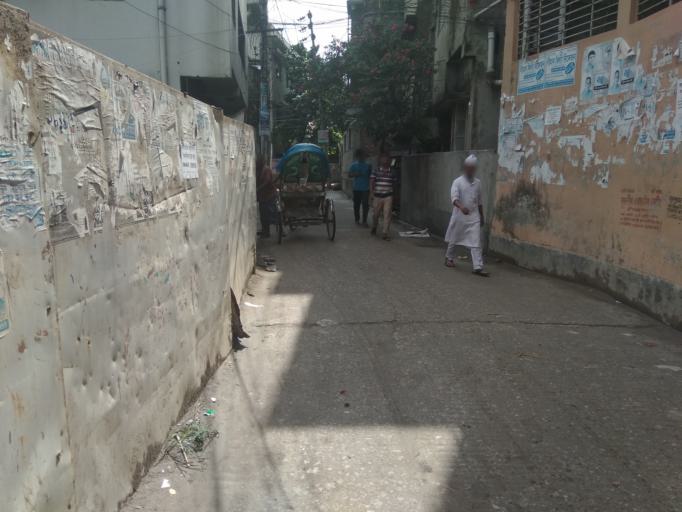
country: BD
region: Dhaka
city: Azimpur
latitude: 23.7971
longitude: 90.3813
